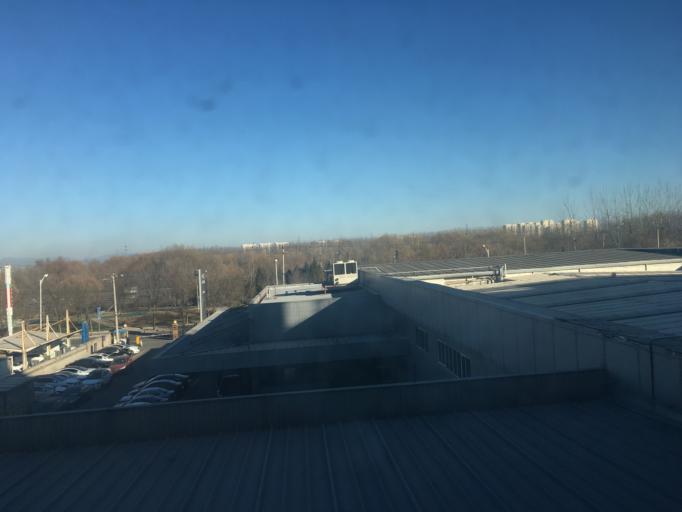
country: CN
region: Beijing
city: Wangjing
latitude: 40.0121
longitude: 116.4732
